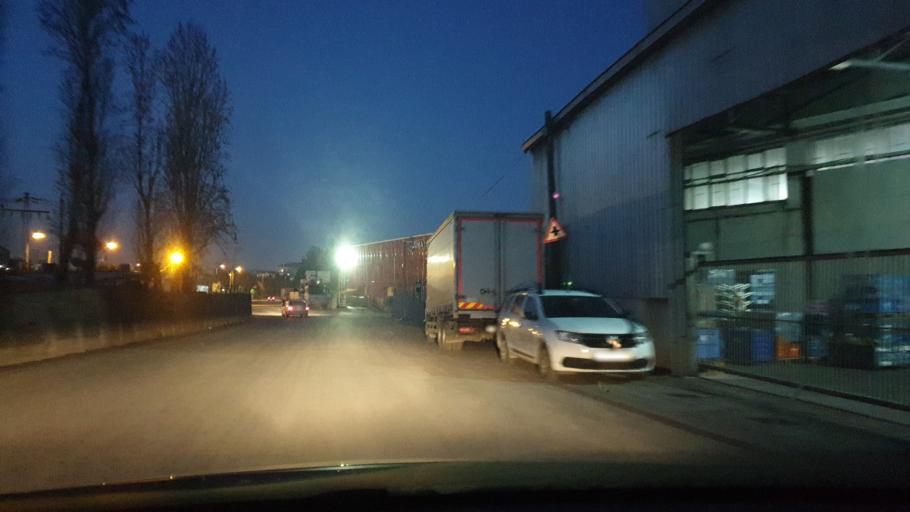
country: TR
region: Istanbul
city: Pendik
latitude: 40.9012
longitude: 29.2950
